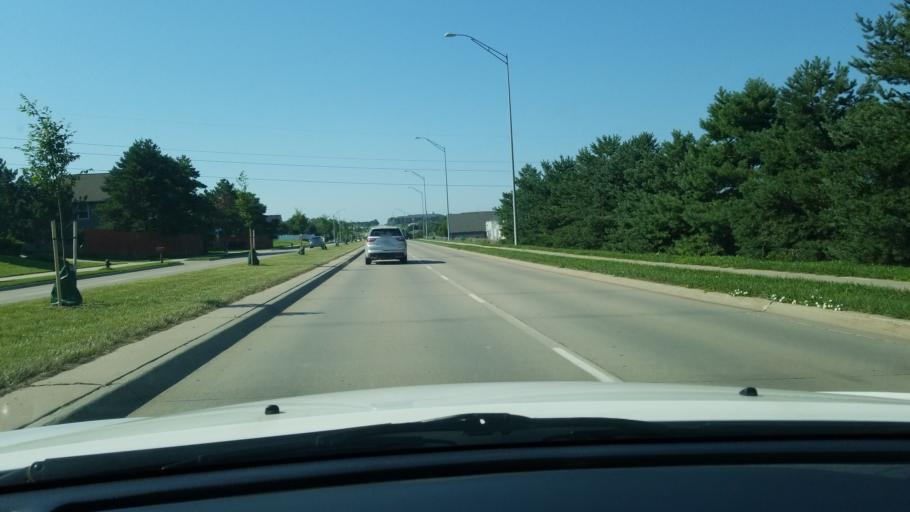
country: US
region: Nebraska
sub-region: Lancaster County
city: Lincoln
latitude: 40.7638
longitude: -96.6062
